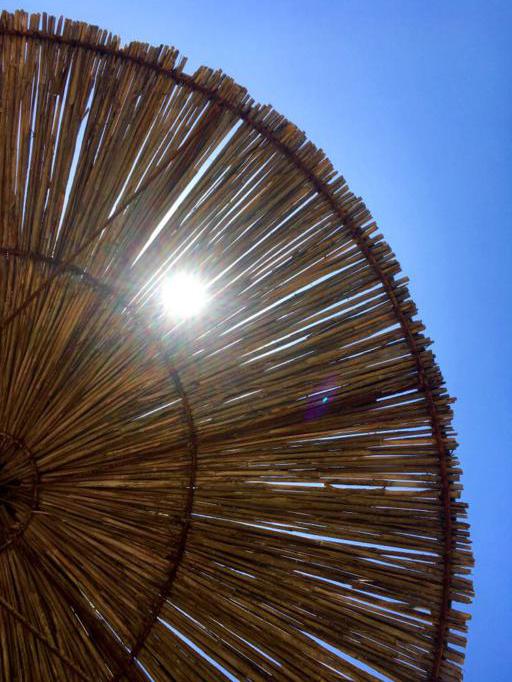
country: AL
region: Tirane
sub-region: Rrethi i Kavajes
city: Golem
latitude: 41.2541
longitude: 19.5235
